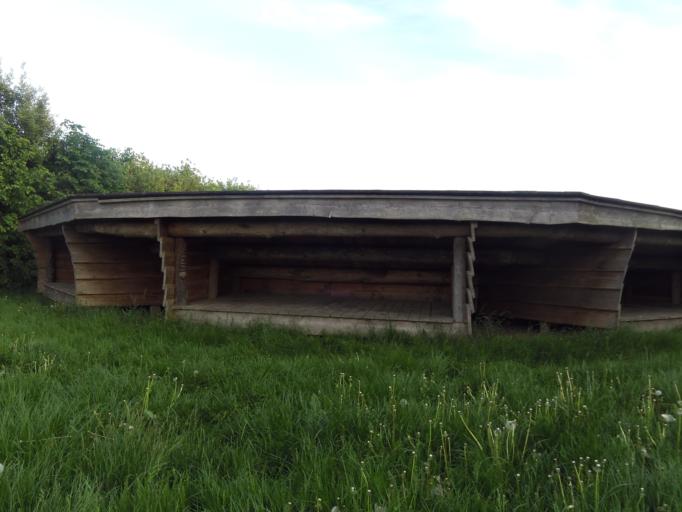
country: DK
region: South Denmark
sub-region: Sonderborg Kommune
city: Broager
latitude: 54.9290
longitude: 9.6727
